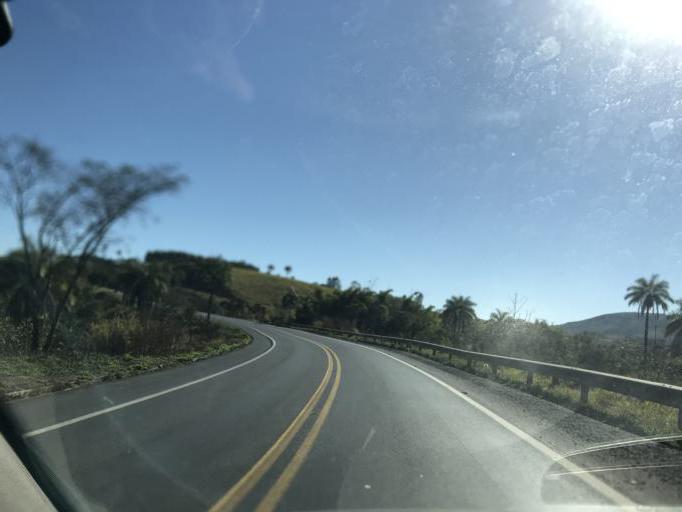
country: BR
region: Minas Gerais
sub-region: Campos Altos
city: Campos Altos
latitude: -19.8178
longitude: -46.0210
